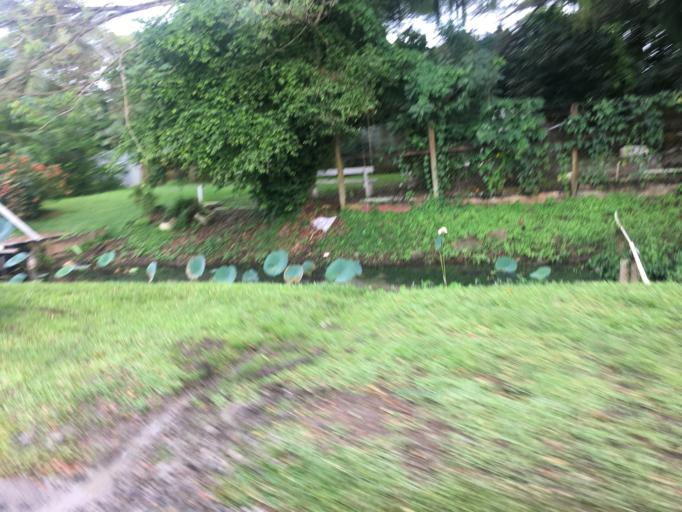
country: GY
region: Demerara-Mahaica
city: Georgetown
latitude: 6.8056
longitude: -58.1317
